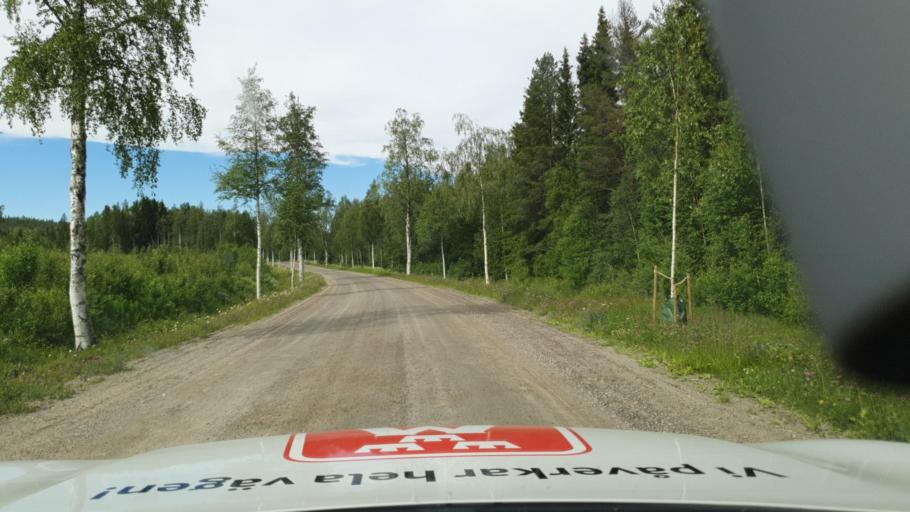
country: SE
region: Vaesterbotten
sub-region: Skelleftea Kommun
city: Burtraesk
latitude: 64.4681
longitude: 20.4600
